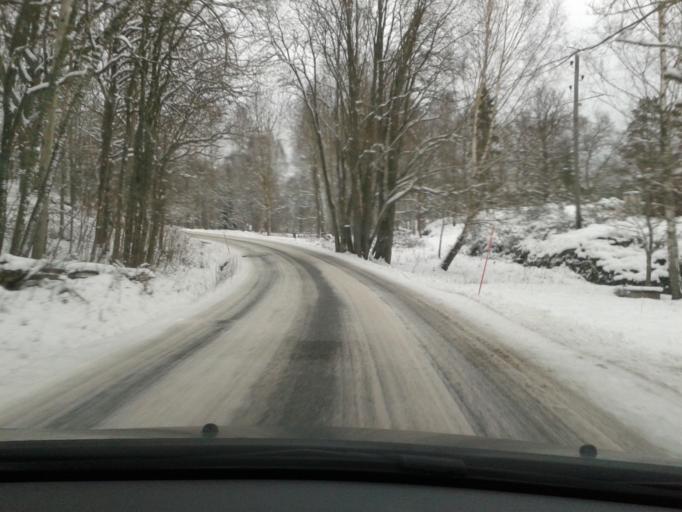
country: SE
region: Stockholm
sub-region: Nacka Kommun
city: Saltsjobaden
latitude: 59.2174
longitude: 18.3061
